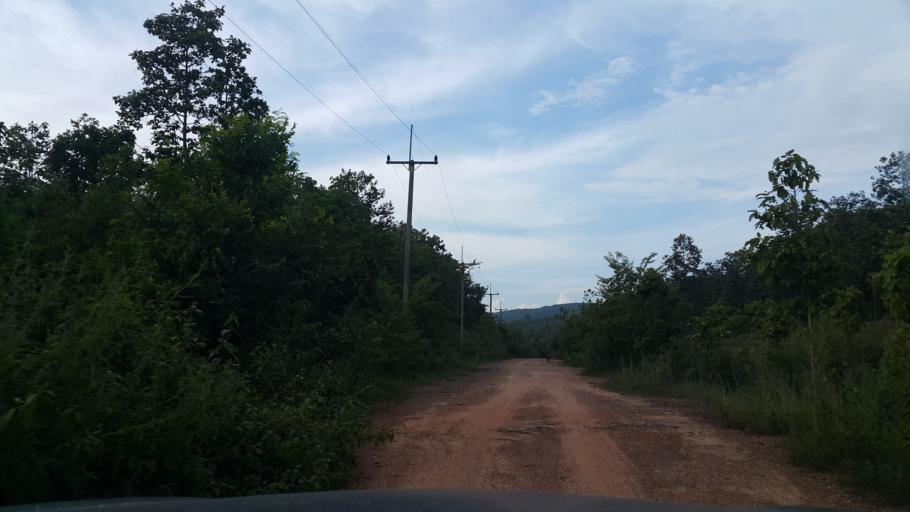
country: TH
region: Chiang Mai
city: San Sai
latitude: 18.9231
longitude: 99.0653
